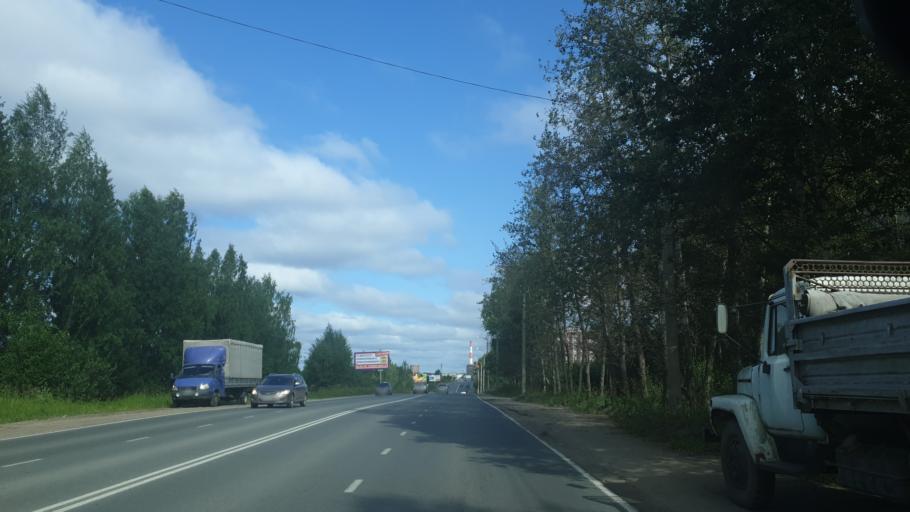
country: RU
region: Komi Republic
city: Ezhva
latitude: 61.7910
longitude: 50.7415
